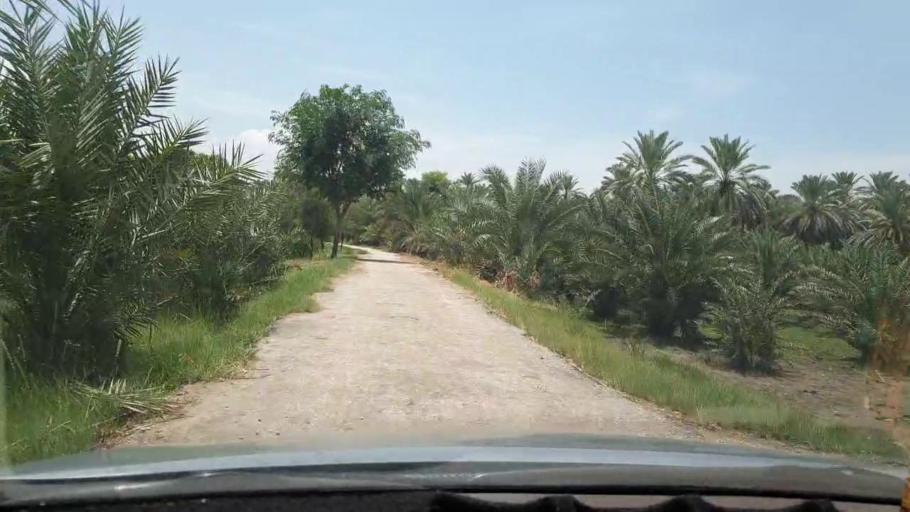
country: PK
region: Sindh
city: Khairpur
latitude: 27.4525
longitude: 68.7806
